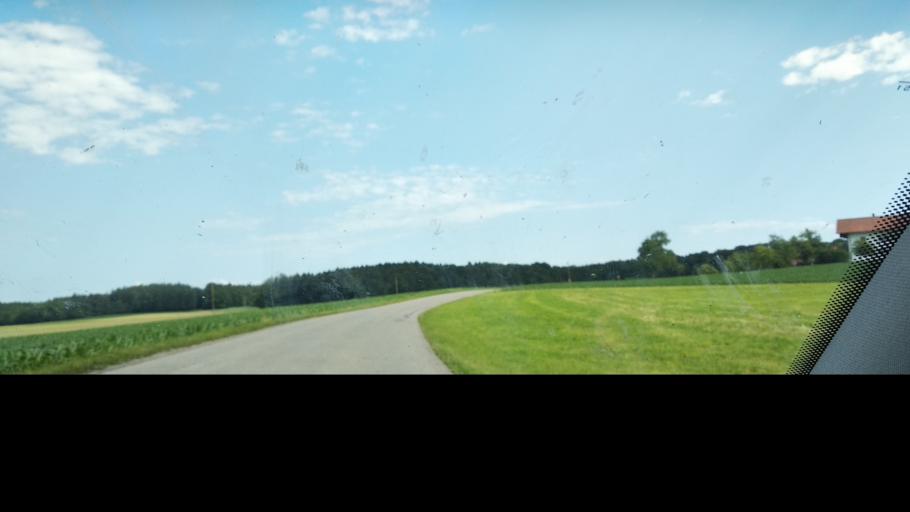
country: DE
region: Bavaria
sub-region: Upper Bavaria
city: Kirchseeon
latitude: 48.0547
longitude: 11.8995
